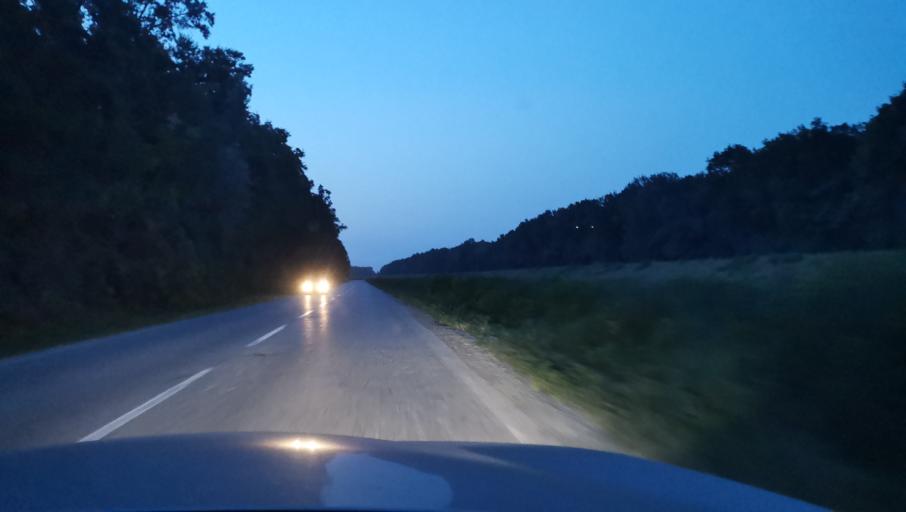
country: RS
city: Boljevci
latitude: 44.6963
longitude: 20.2002
